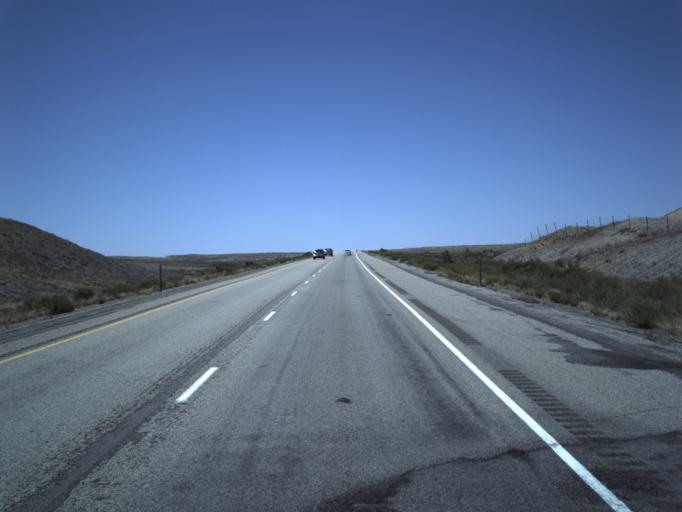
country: US
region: Utah
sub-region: Grand County
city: Moab
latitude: 38.9743
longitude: -109.3580
